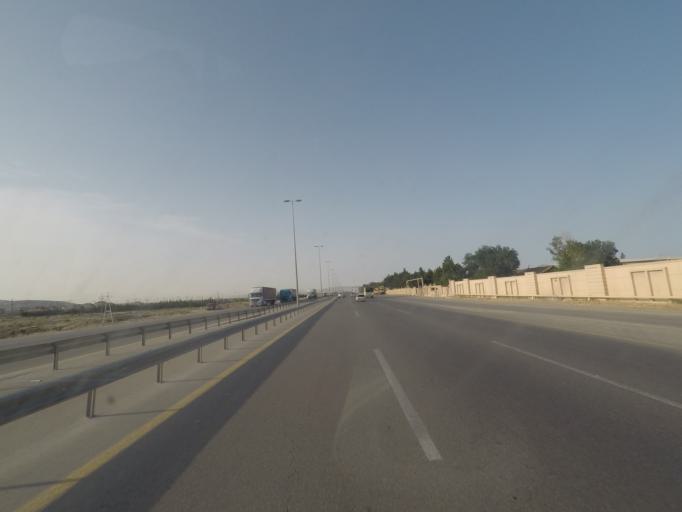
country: AZ
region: Baki
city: Qobustan
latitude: 40.0961
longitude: 49.4216
